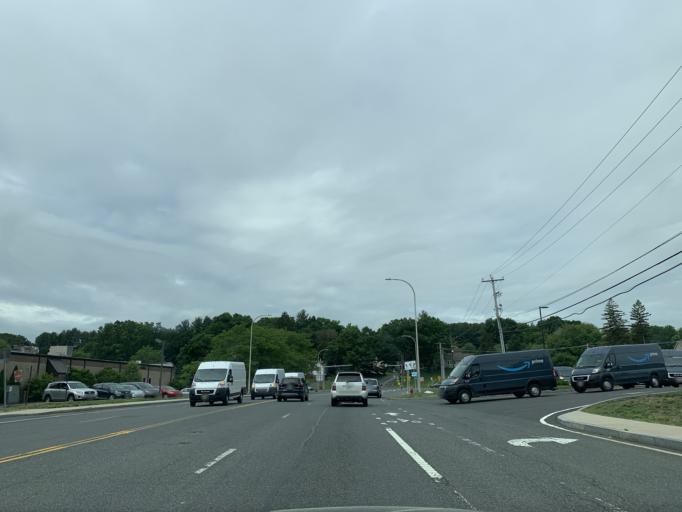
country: US
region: Massachusetts
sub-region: Hampden County
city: Holyoke
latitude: 42.1741
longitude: -72.6463
